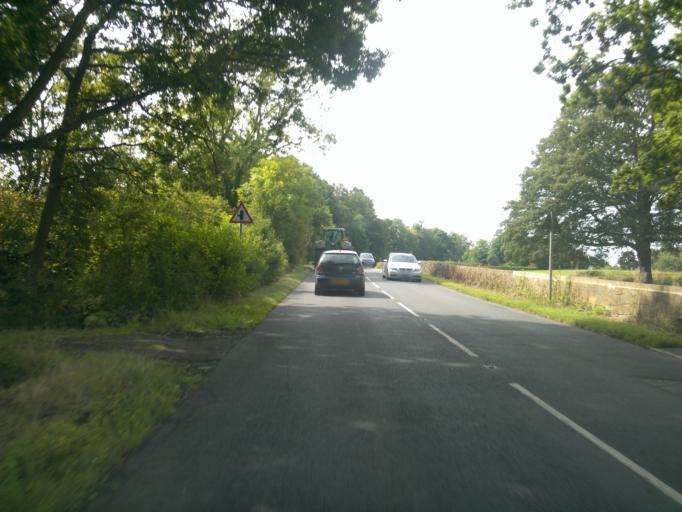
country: GB
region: England
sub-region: Kent
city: Tonbridge
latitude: 51.2012
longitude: 0.2193
